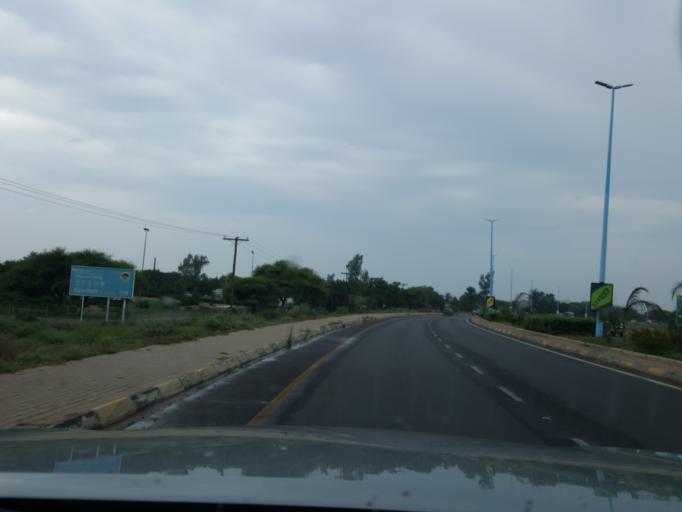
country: BW
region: South East
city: Gaborone
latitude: -24.6157
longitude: 25.9301
